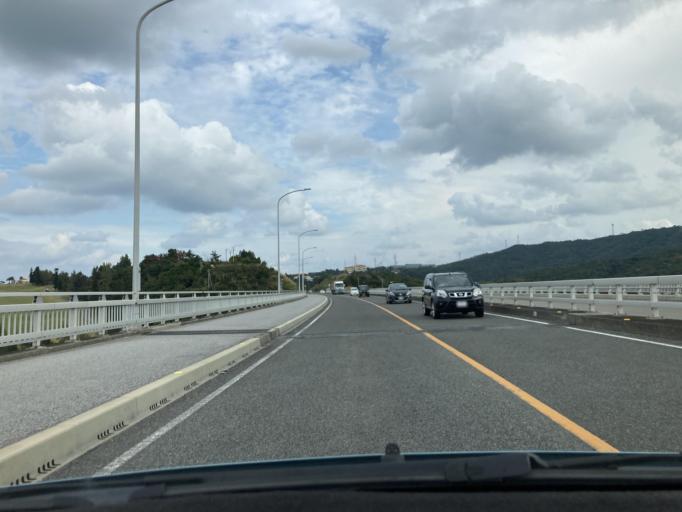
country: JP
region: Okinawa
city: Ishikawa
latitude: 26.4497
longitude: 127.8174
